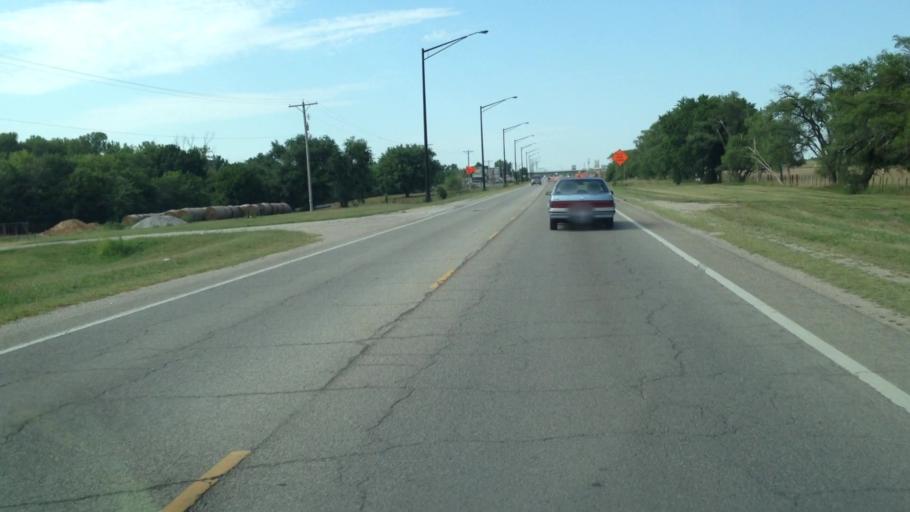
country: US
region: Kansas
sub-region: Labette County
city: Parsons
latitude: 37.3578
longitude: -95.2587
